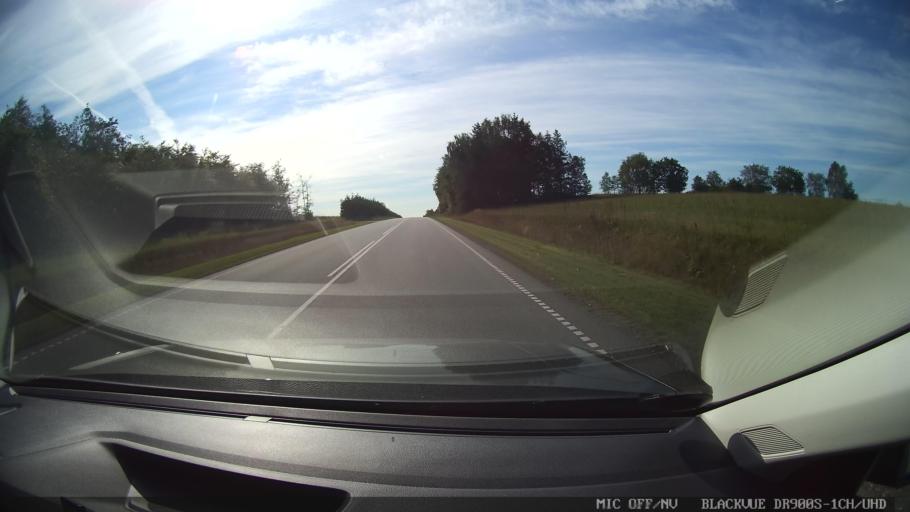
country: DK
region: North Denmark
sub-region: Mariagerfjord Kommune
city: Hadsund
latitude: 56.7667
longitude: 10.0635
